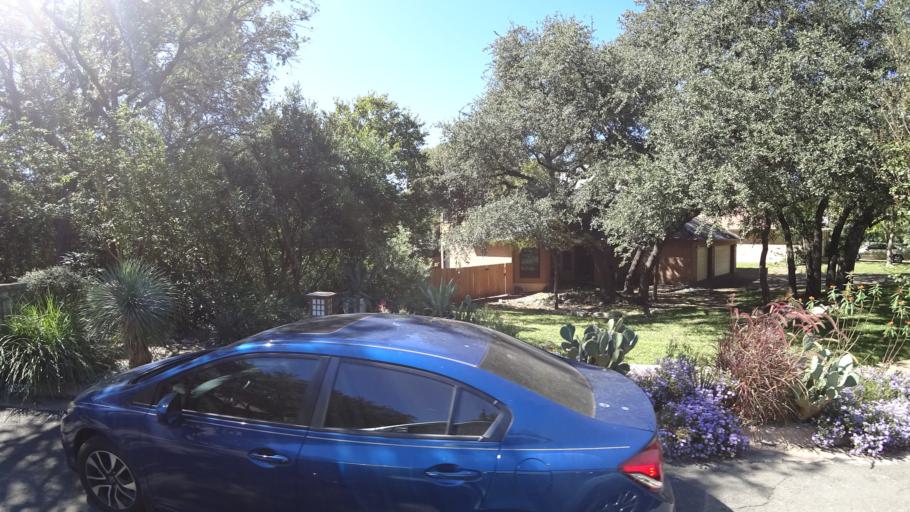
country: US
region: Texas
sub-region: Travis County
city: West Lake Hills
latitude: 30.3406
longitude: -97.7805
